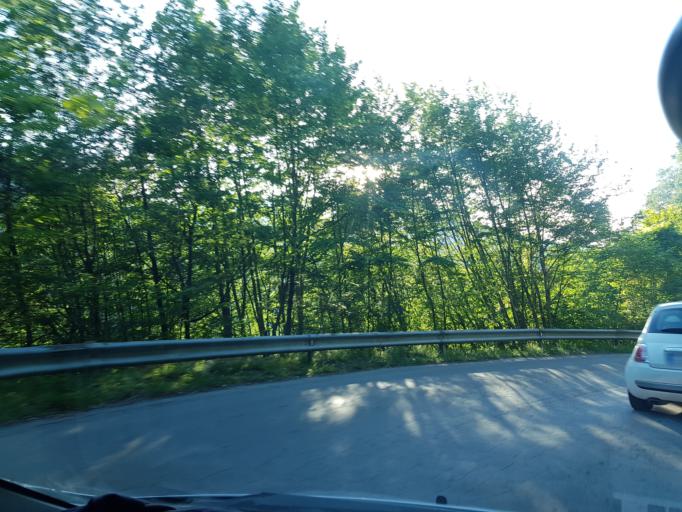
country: IT
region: Tuscany
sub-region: Provincia di Lucca
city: Minucciano
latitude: 44.1816
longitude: 10.1967
